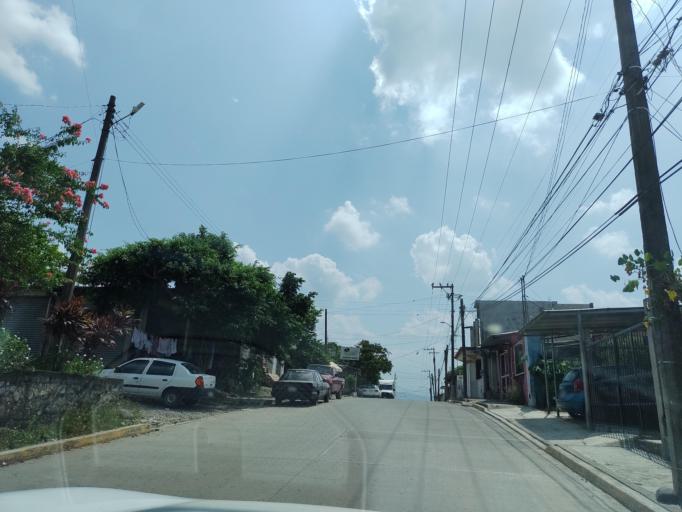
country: MX
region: Veracruz
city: Martinez de la Torre
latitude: 20.0762
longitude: -97.0467
